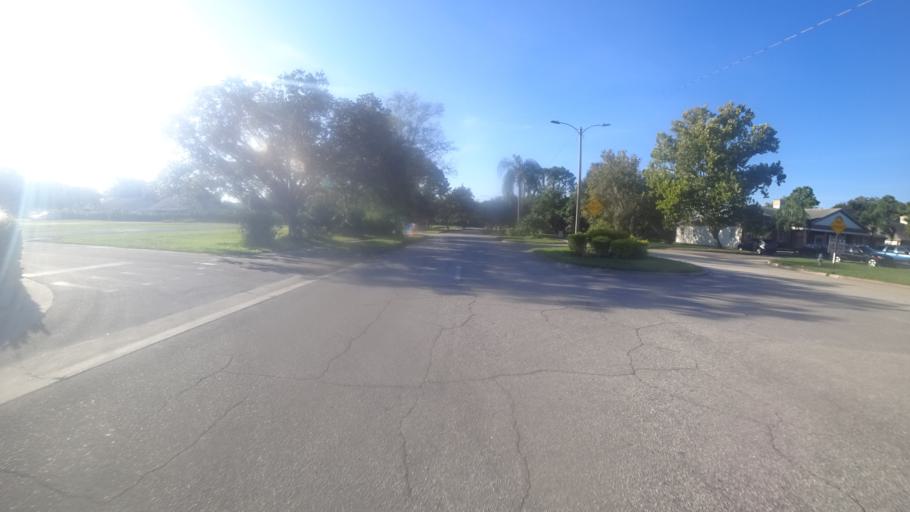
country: US
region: Florida
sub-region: Manatee County
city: Ellenton
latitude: 27.4963
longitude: -82.5018
